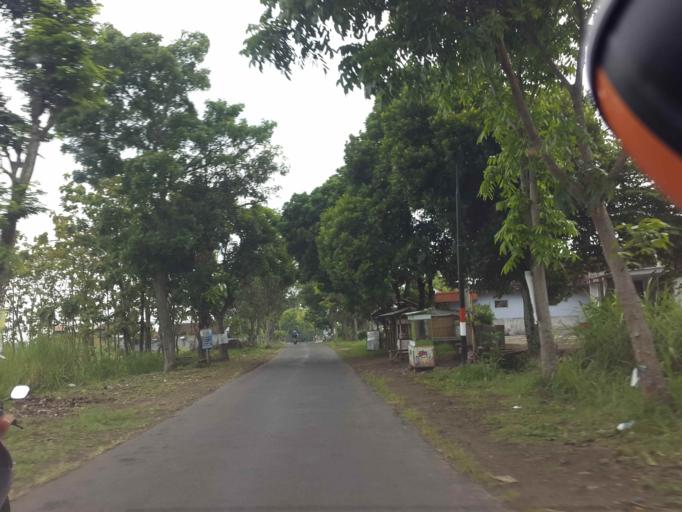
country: ID
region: East Java
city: Madiun
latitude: -7.6696
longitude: 111.3106
